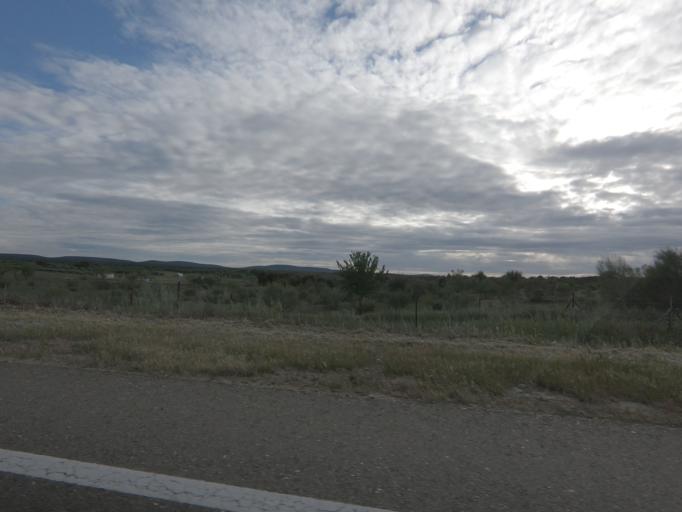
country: ES
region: Extremadura
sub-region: Provincia de Caceres
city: Torrejoncillo
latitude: 39.8887
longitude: -6.4796
